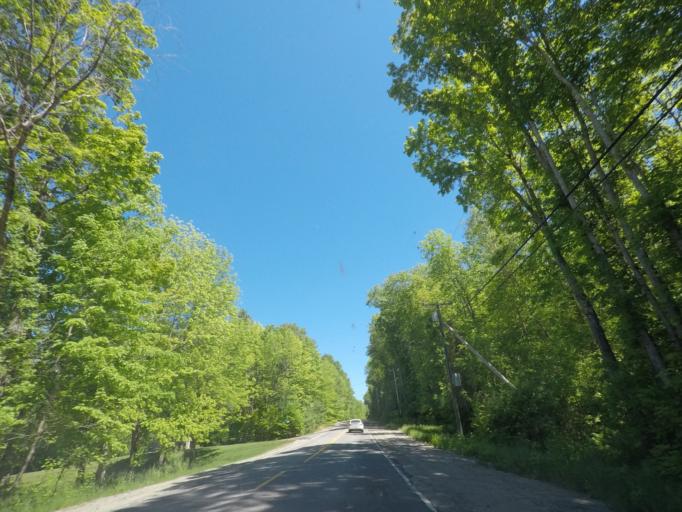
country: US
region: Maine
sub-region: Kennebec County
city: Manchester
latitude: 44.2900
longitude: -69.8891
